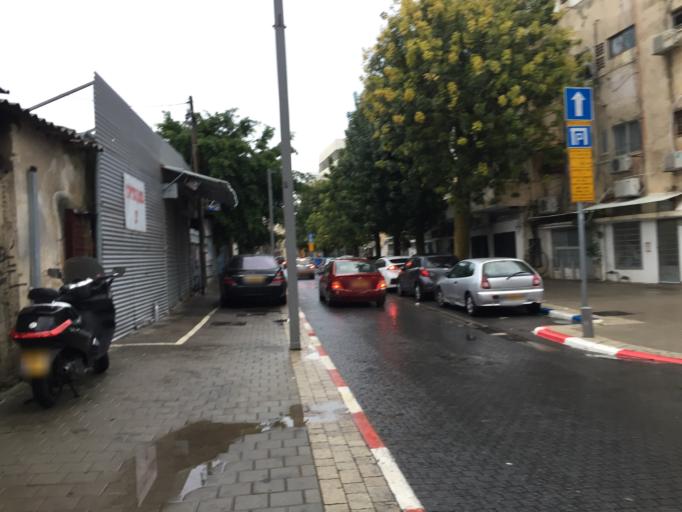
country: IL
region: Tel Aviv
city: Yafo
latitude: 32.0518
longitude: 34.7583
